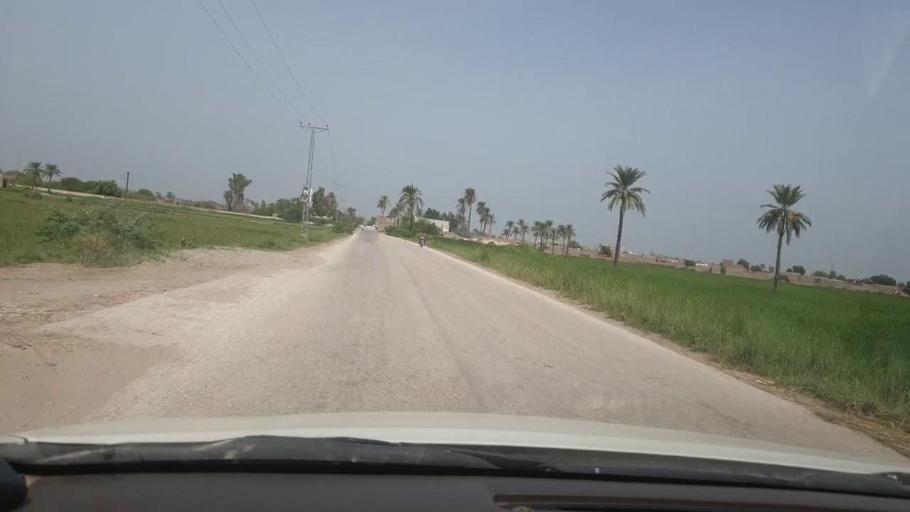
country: PK
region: Sindh
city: Shikarpur
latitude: 27.9517
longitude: 68.6168
